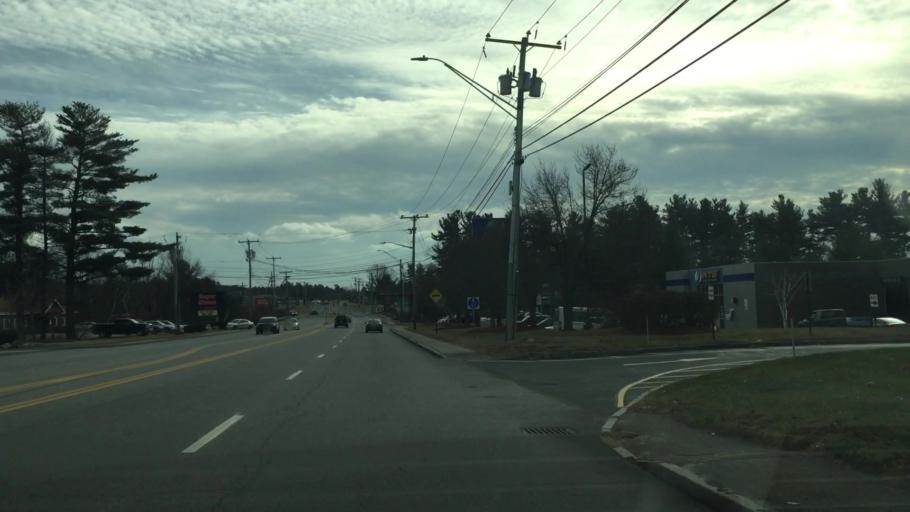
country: US
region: New Hampshire
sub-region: Hillsborough County
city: Manchester
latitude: 42.9487
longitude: -71.4340
